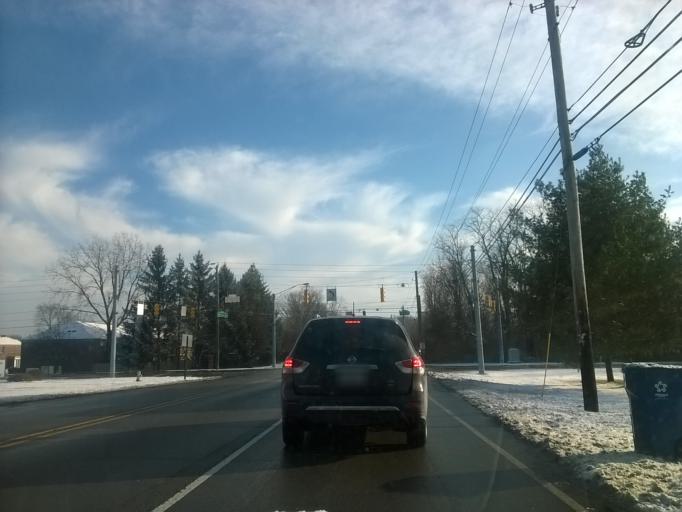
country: US
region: Indiana
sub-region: Marion County
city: Meridian Hills
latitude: 39.9203
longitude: -86.1459
